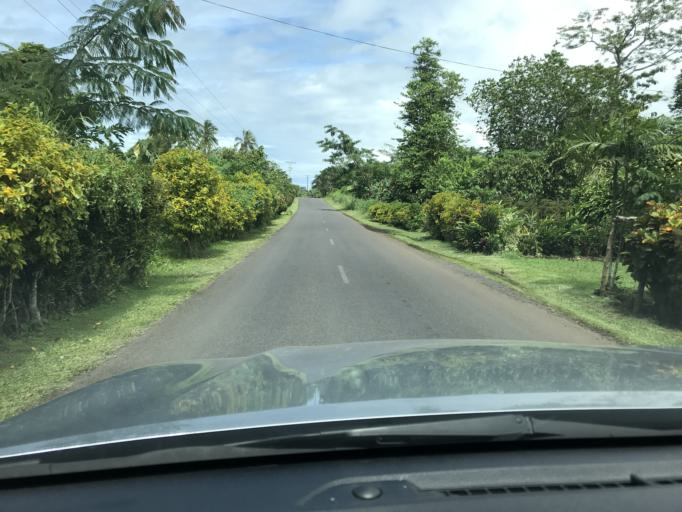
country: WS
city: Fasito`outa
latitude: -13.8578
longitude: -171.9005
